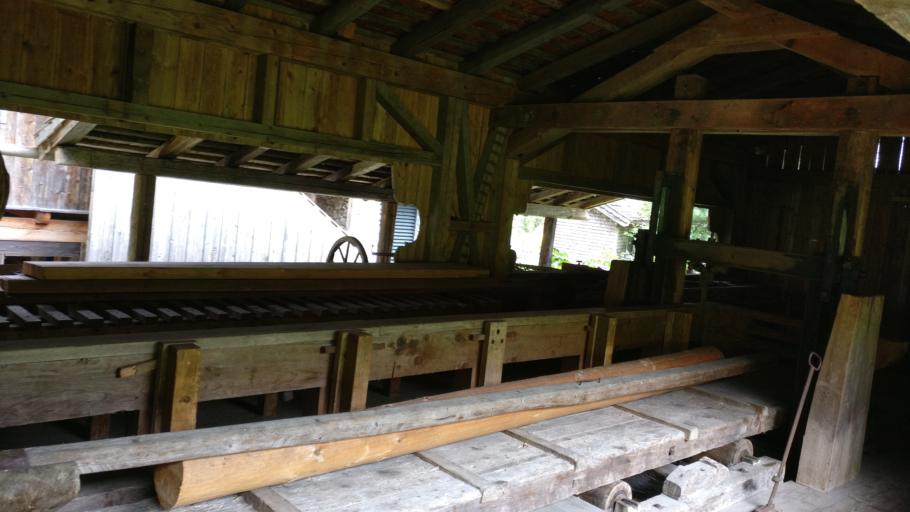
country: AT
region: Salzburg
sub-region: Politischer Bezirk Zell am See
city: Bramberg am Wildkogel
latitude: 47.2704
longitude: 12.3380
